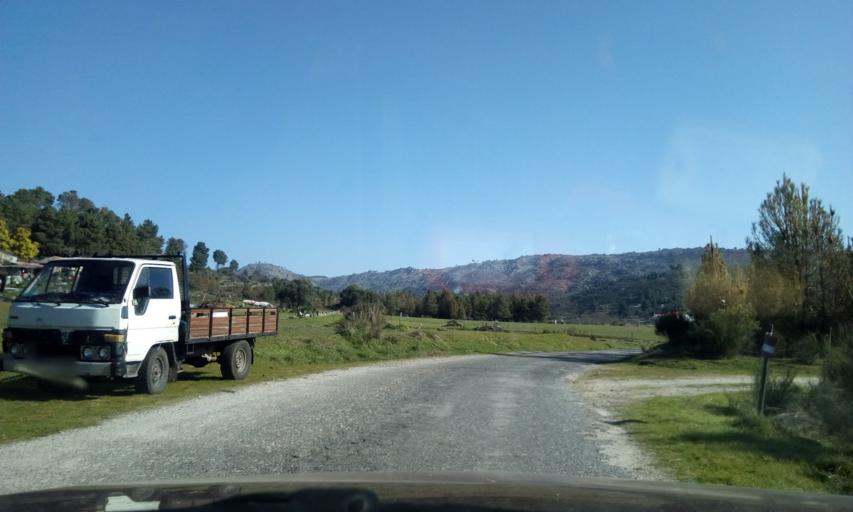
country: PT
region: Guarda
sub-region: Celorico da Beira
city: Celorico da Beira
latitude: 40.6853
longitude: -7.4063
